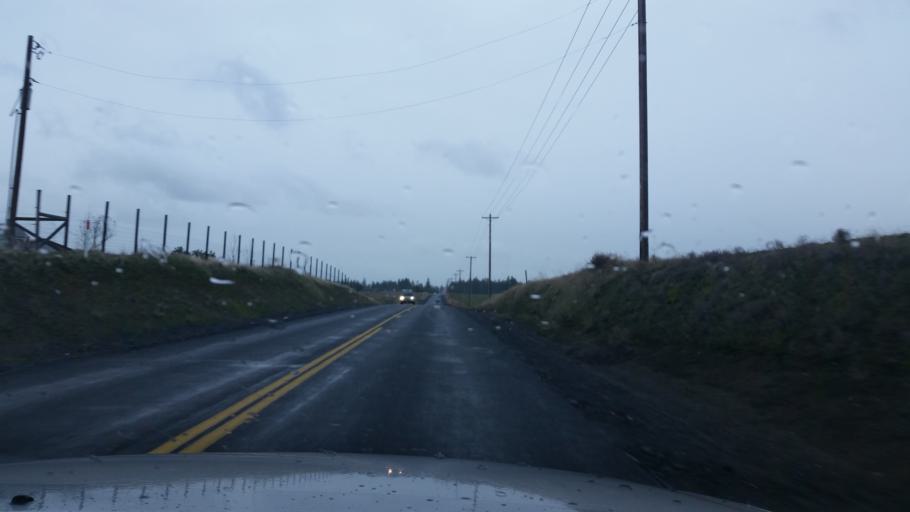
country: US
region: Washington
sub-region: Spokane County
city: Airway Heights
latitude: 47.6719
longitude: -117.6010
